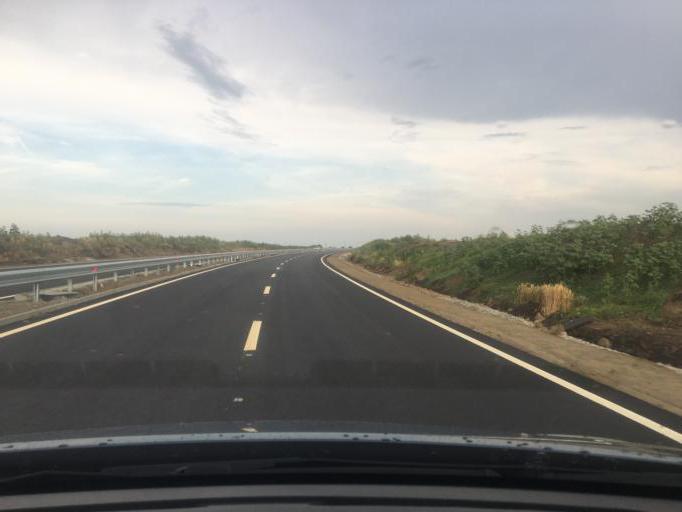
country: BG
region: Burgas
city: Aheloy
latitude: 42.6557
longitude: 27.6582
